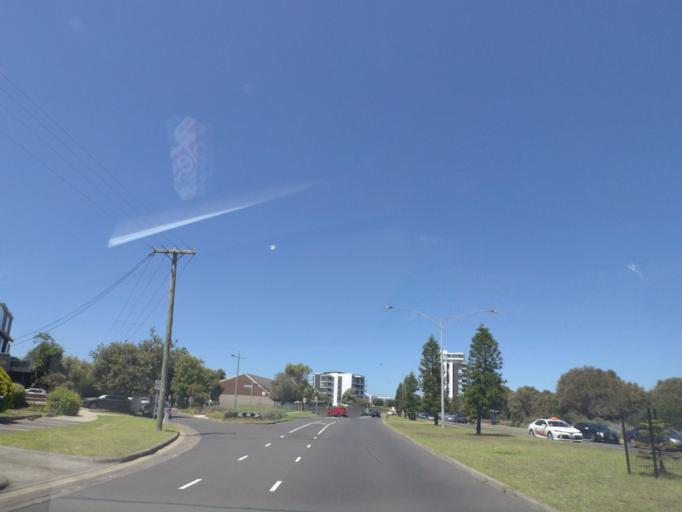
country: AU
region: Victoria
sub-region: Port Phillip
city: Port Melbourne
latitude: -37.8390
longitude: 144.9228
